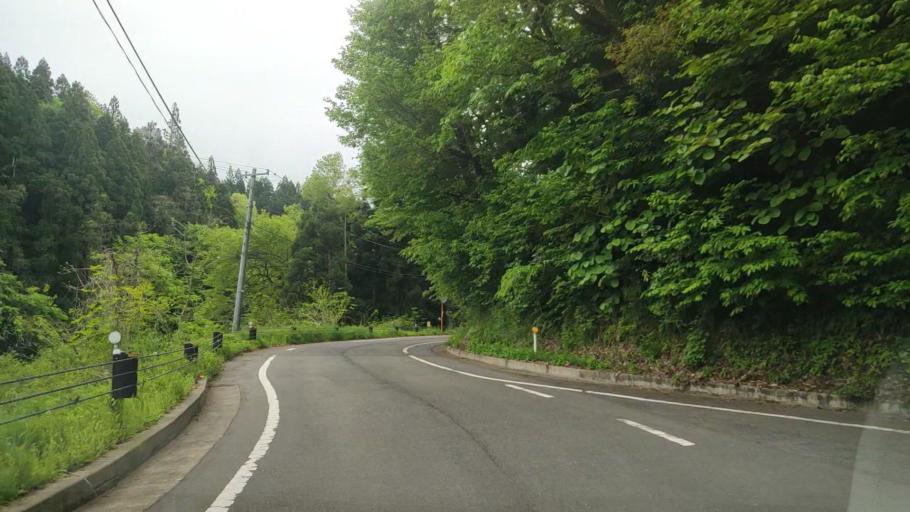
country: JP
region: Niigata
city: Gosen
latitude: 37.7157
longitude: 139.1240
